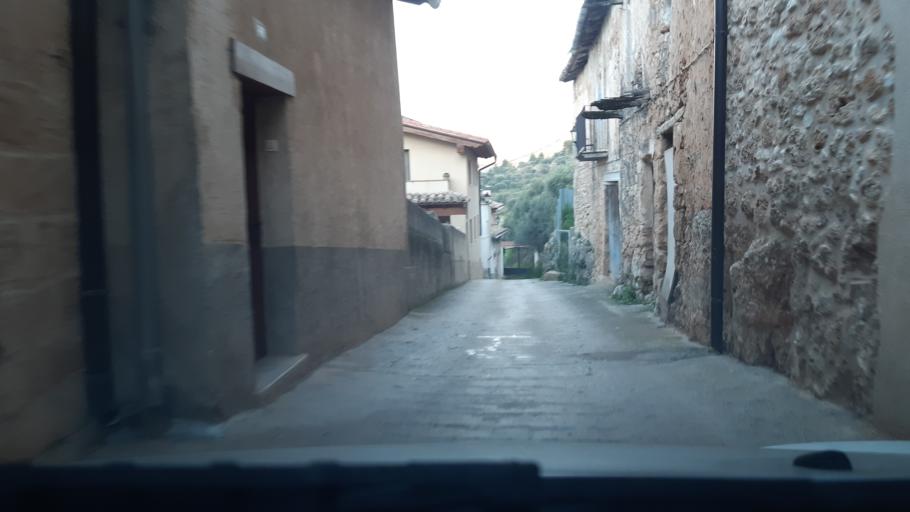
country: ES
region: Aragon
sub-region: Provincia de Teruel
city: Valderrobres
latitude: 40.8325
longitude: 0.1837
